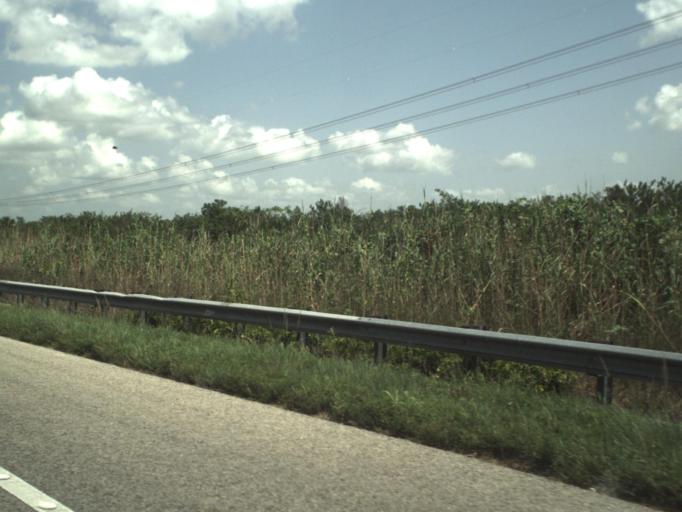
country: US
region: Florida
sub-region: Broward County
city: Weston
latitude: 26.2501
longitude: -80.4722
